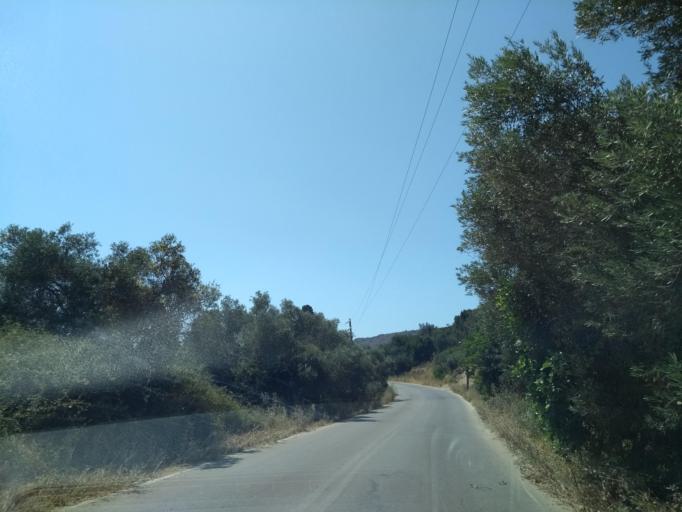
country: GR
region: Crete
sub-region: Nomos Chanias
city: Georgioupolis
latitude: 35.3797
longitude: 24.2431
